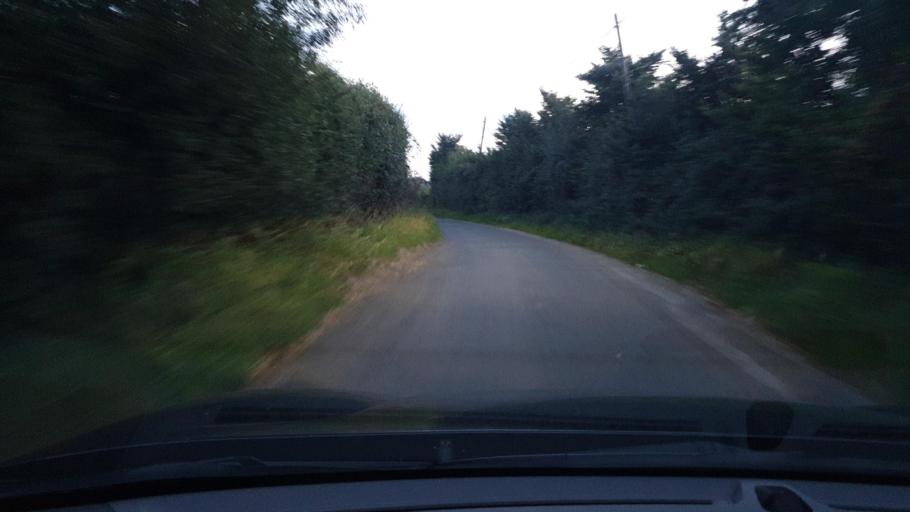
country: IE
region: Leinster
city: Lusk
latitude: 53.5317
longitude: -6.1377
